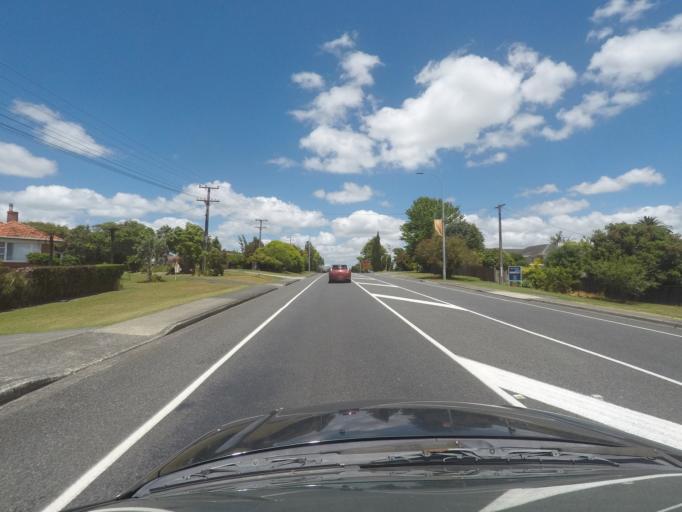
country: NZ
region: Northland
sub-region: Whangarei
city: Whangarei
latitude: -35.7473
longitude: 174.3673
